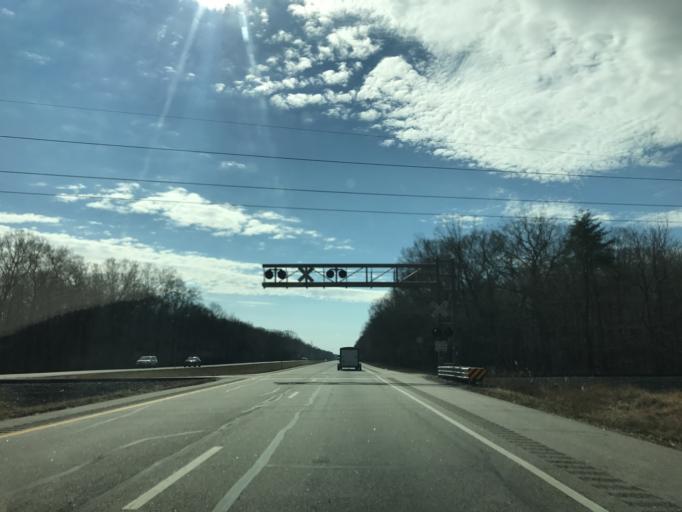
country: US
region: Delaware
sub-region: New Castle County
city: Townsend
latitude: 39.3123
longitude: -75.8488
